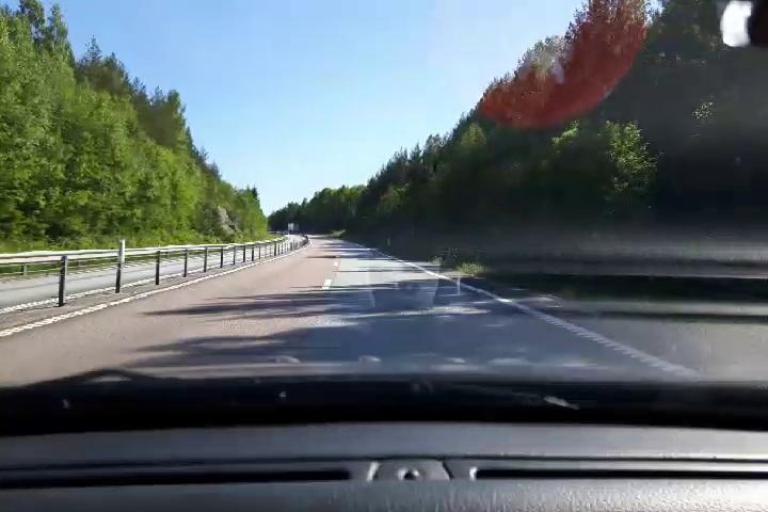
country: SE
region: Gaevleborg
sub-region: Soderhamns Kommun
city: Soderhamn
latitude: 61.2726
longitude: 17.0263
